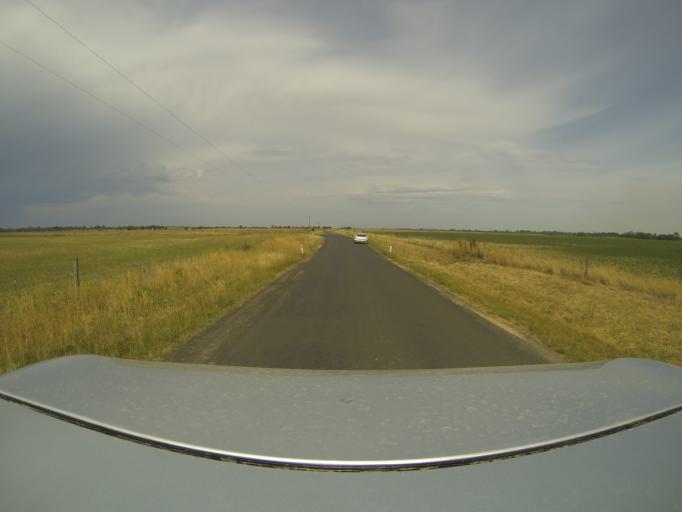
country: AU
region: Victoria
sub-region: Wellington
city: Heyfield
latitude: -37.9986
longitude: 146.6901
